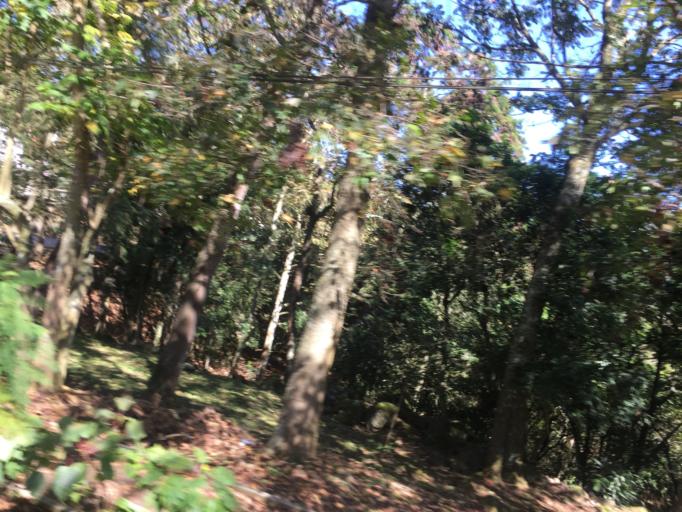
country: MX
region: Veracruz
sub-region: Xalapa
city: Xalapa de Enriquez
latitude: 19.5325
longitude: -96.8932
